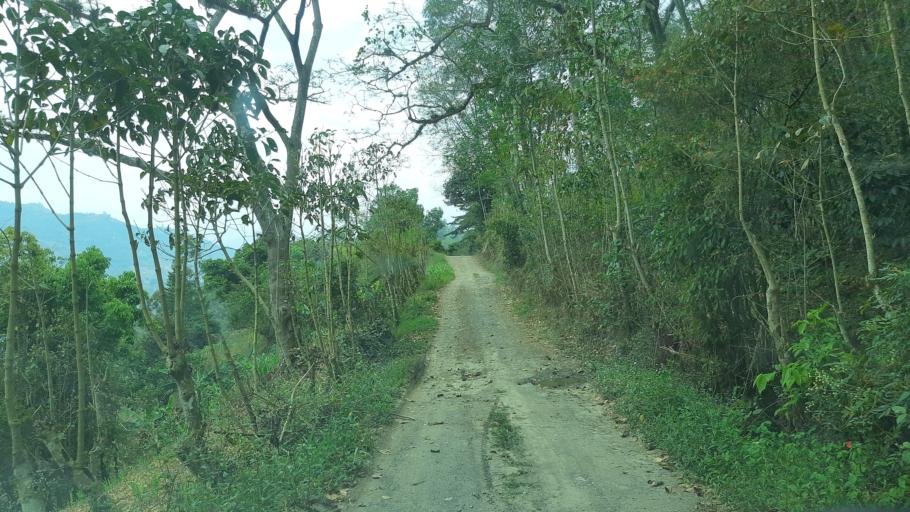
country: CO
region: Boyaca
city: Garagoa
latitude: 5.0824
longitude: -73.3905
